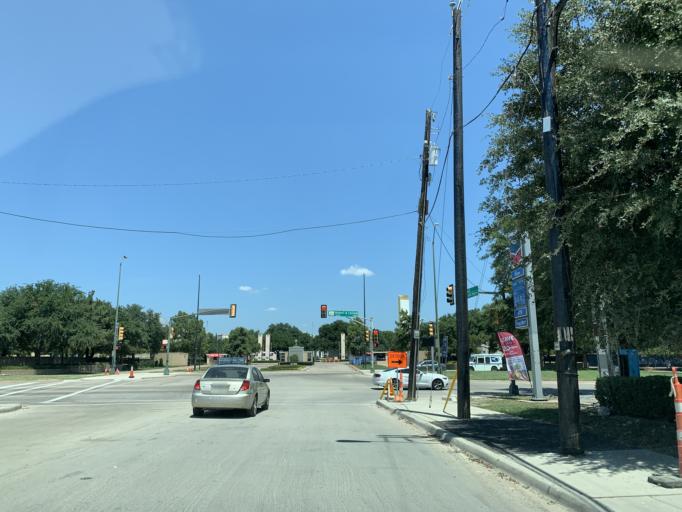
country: US
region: Texas
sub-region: Dallas County
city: Dallas
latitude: 32.7772
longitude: -96.7655
